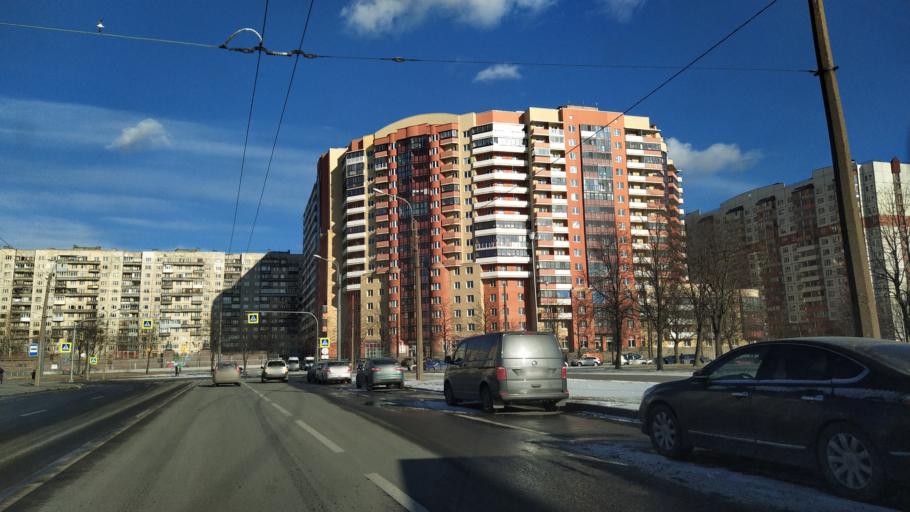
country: RU
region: Leningrad
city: Kalininskiy
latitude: 59.9679
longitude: 30.4257
